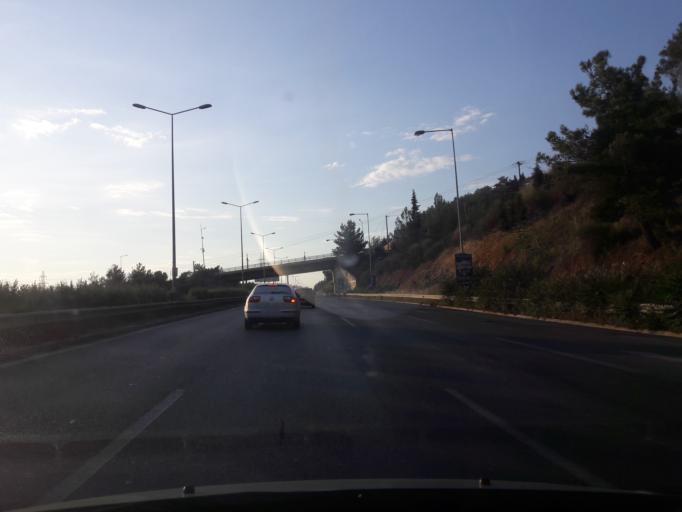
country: GR
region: Central Macedonia
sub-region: Nomos Thessalonikis
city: Agios Pavlos
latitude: 40.6330
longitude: 22.9735
